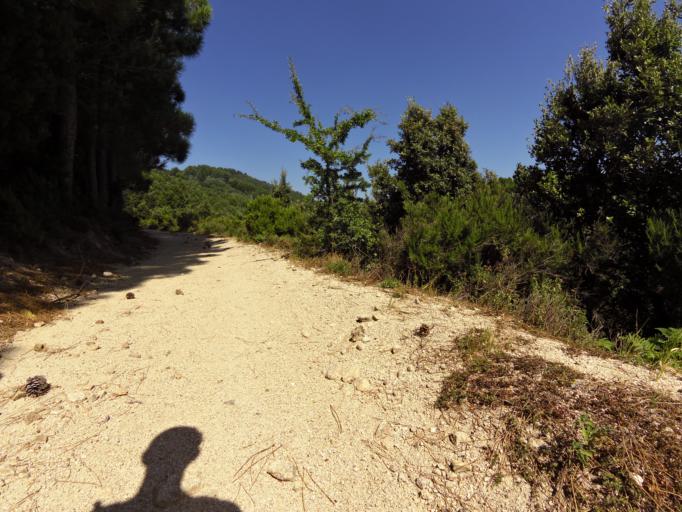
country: IT
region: Calabria
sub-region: Provincia di Reggio Calabria
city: Bivongi
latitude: 38.5099
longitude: 16.4347
